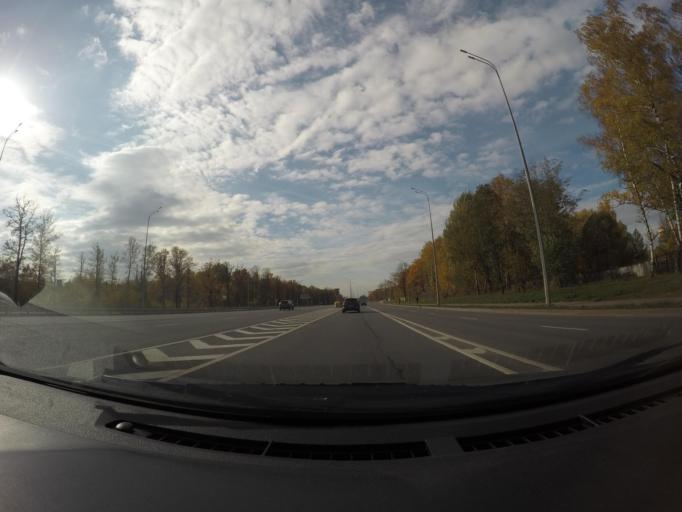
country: RU
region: Moscow
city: Severnyy
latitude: 55.9225
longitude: 37.5226
